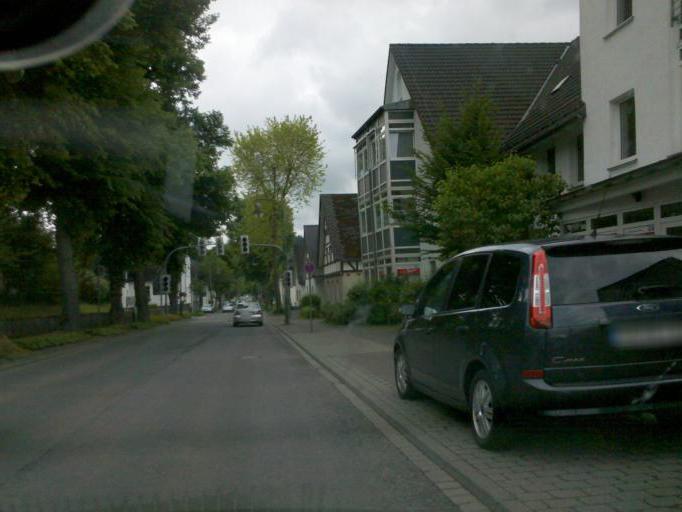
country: DE
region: North Rhine-Westphalia
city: Eslohe
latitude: 51.2572
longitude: 8.1742
